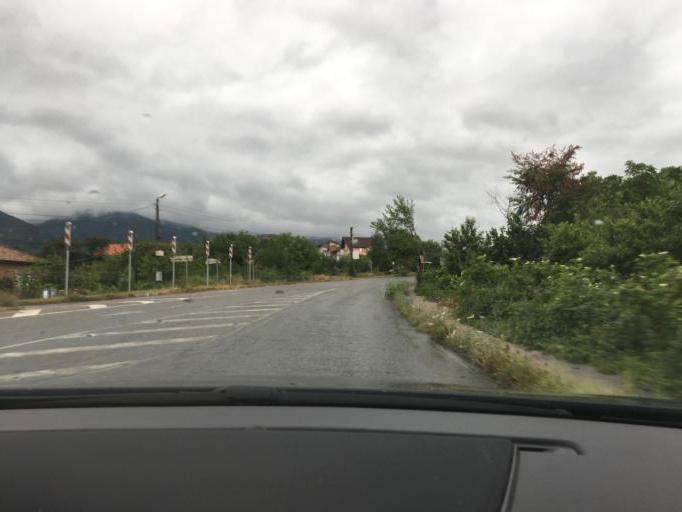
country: BG
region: Kyustendil
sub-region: Obshtina Kyustendil
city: Kyustendil
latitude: 42.2732
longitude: 22.6538
